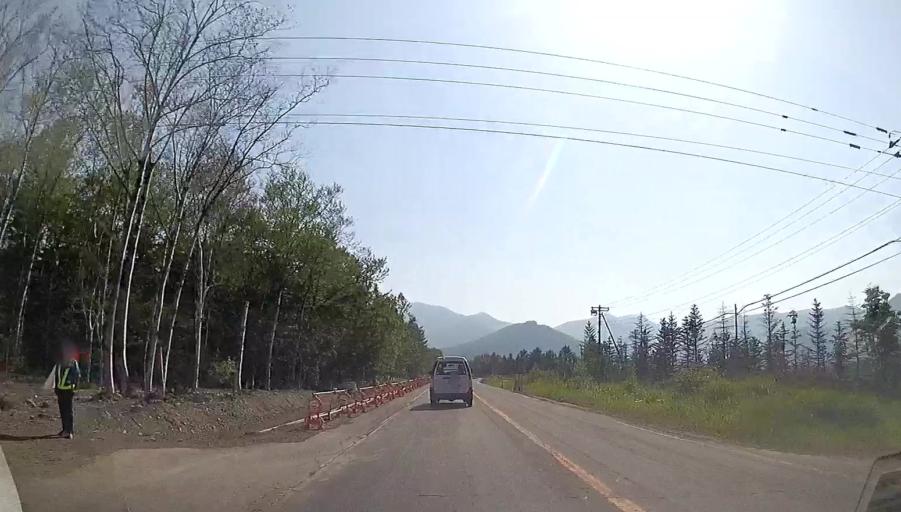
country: JP
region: Hokkaido
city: Otofuke
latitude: 42.9819
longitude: 142.8351
